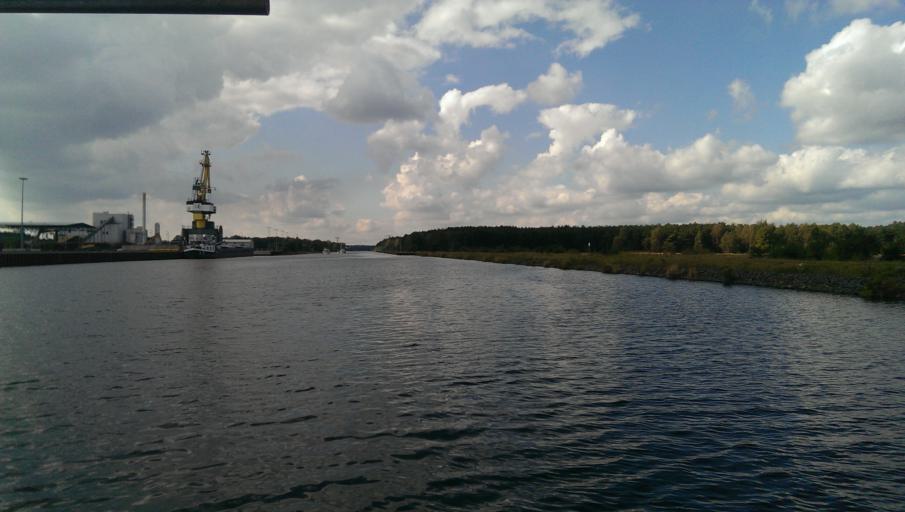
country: DE
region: Brandenburg
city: Eberswalde
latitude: 52.8531
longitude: 13.7862
